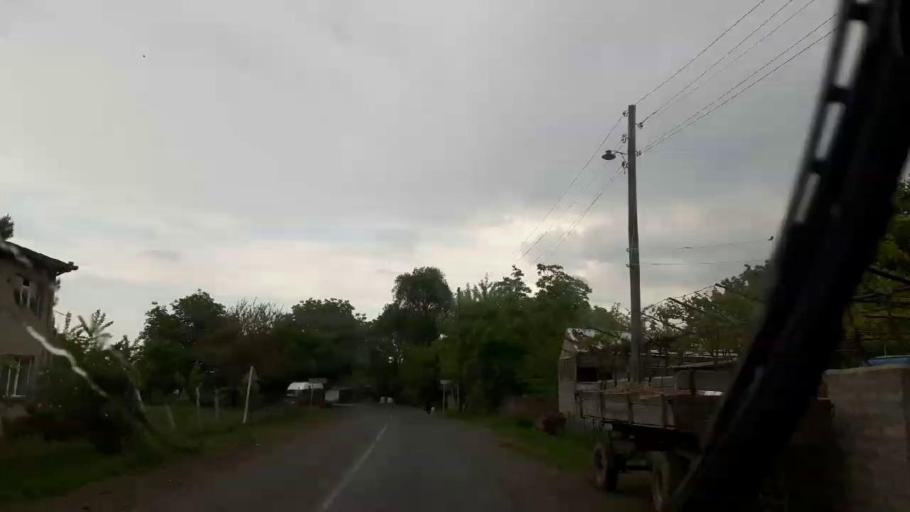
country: GE
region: Shida Kartli
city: Gori
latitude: 41.9598
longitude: 44.2118
